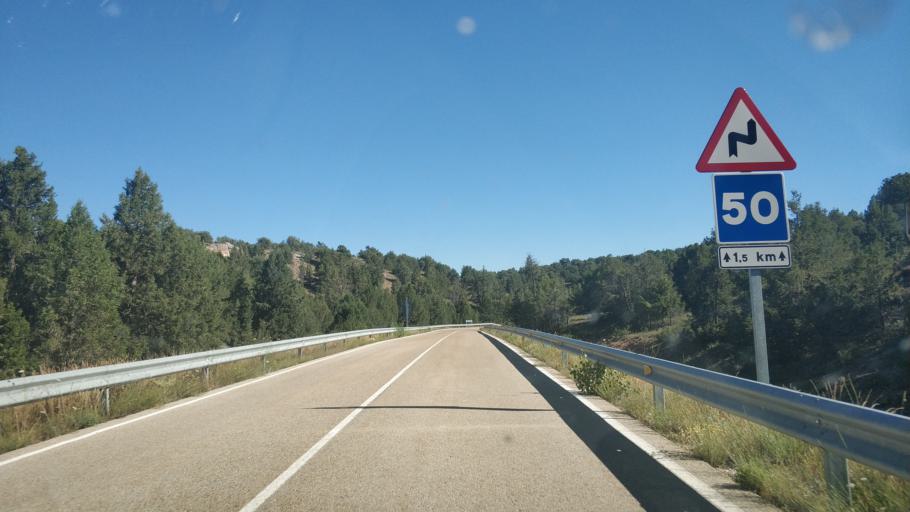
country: ES
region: Castille and Leon
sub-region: Provincia de Soria
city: Montejo de Tiermes
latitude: 41.4330
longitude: -3.2048
